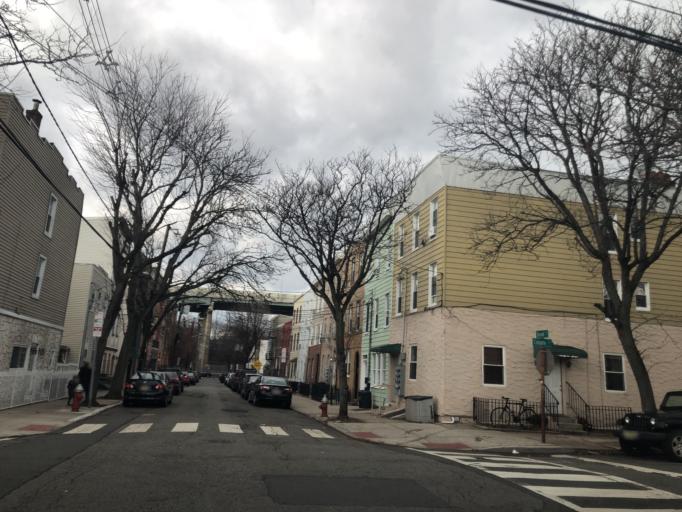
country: US
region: New Jersey
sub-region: Hudson County
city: Jersey City
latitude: 40.7235
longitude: -74.0522
